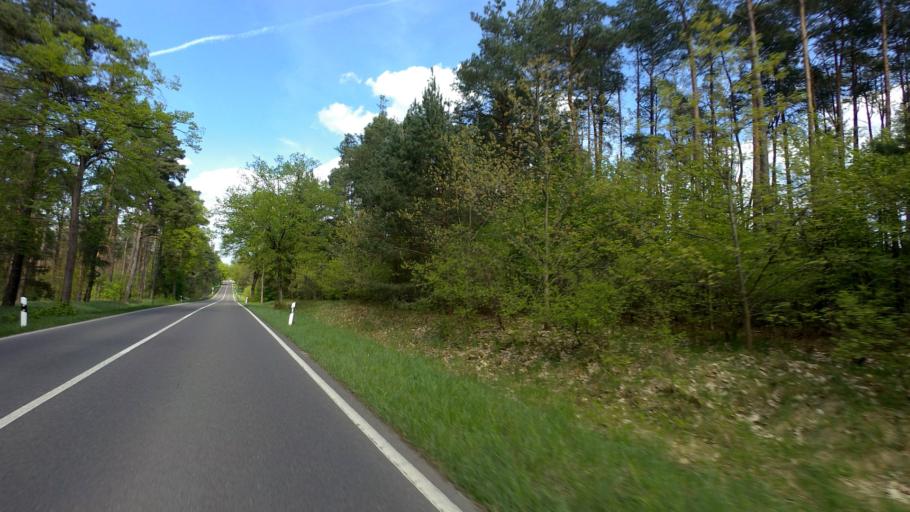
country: DE
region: Brandenburg
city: Milmersdorf
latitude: 53.0843
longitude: 13.6242
